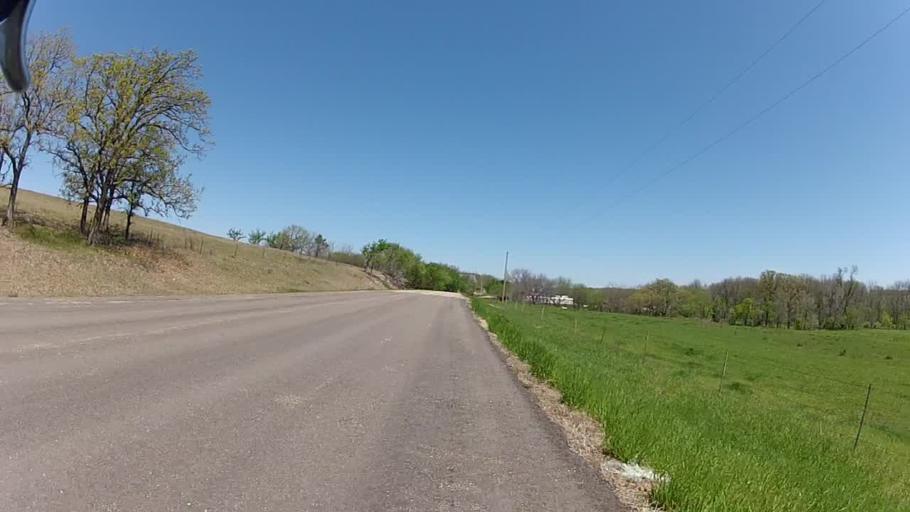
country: US
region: Kansas
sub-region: Riley County
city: Ogden
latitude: 38.9953
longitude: -96.5976
